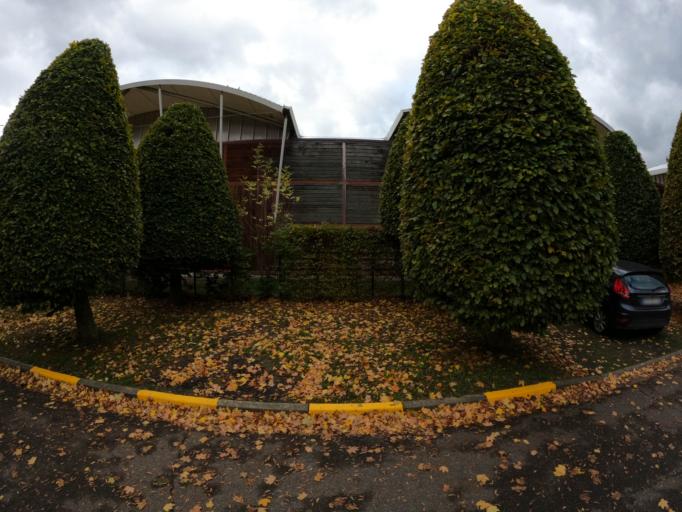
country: FR
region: Ile-de-France
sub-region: Departement de Seine-et-Marne
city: Coupvray
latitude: 48.8985
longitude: 2.7871
